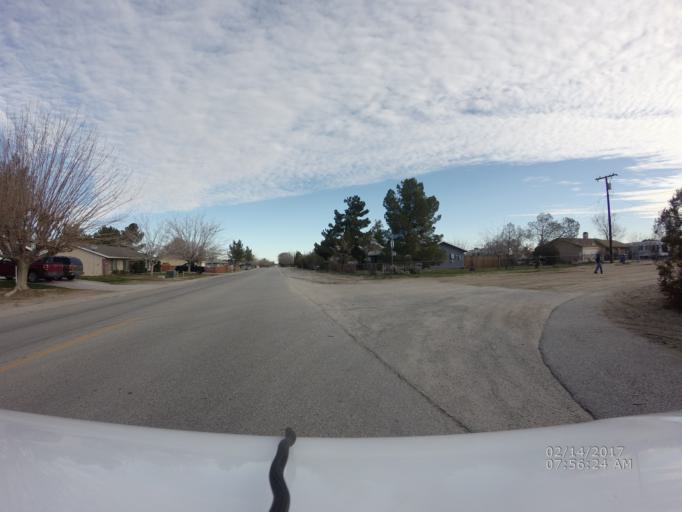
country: US
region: California
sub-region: Los Angeles County
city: Littlerock
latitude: 34.5519
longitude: -117.9581
